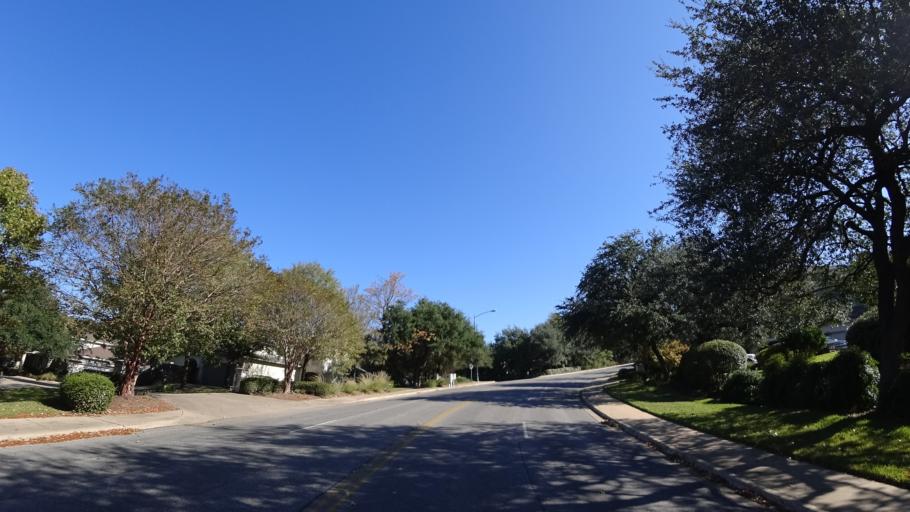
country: US
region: Texas
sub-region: Williamson County
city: Jollyville
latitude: 30.4050
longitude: -97.7512
